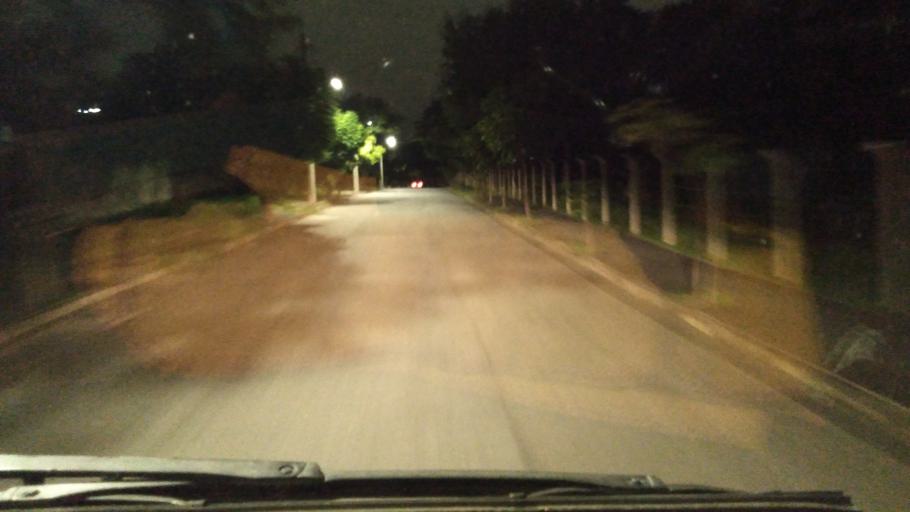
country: BR
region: Minas Gerais
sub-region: Belo Horizonte
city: Belo Horizonte
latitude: -19.8939
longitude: -43.9740
